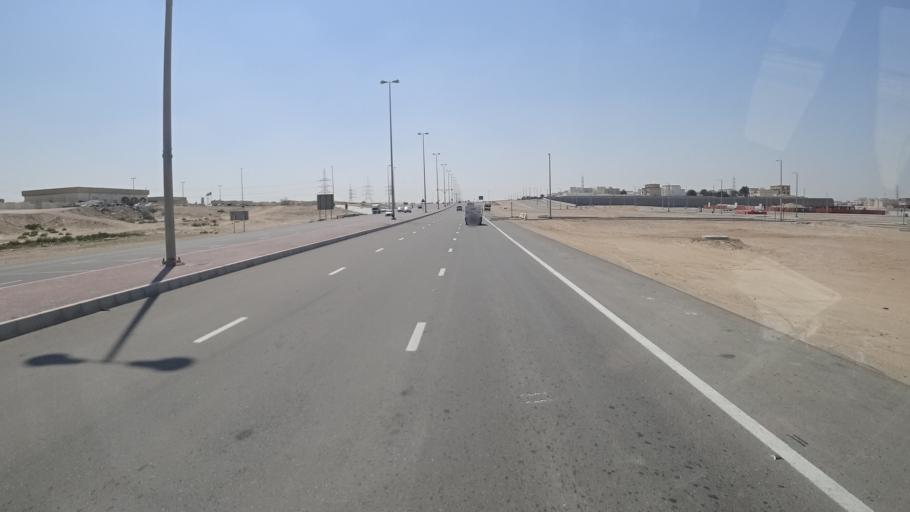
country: AE
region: Abu Dhabi
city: Abu Dhabi
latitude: 24.3021
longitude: 54.6670
